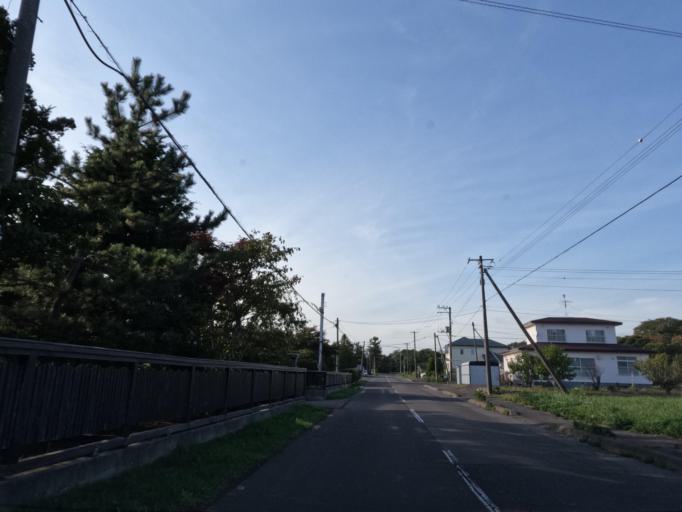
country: JP
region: Hokkaido
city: Date
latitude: 42.4228
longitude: 140.9087
